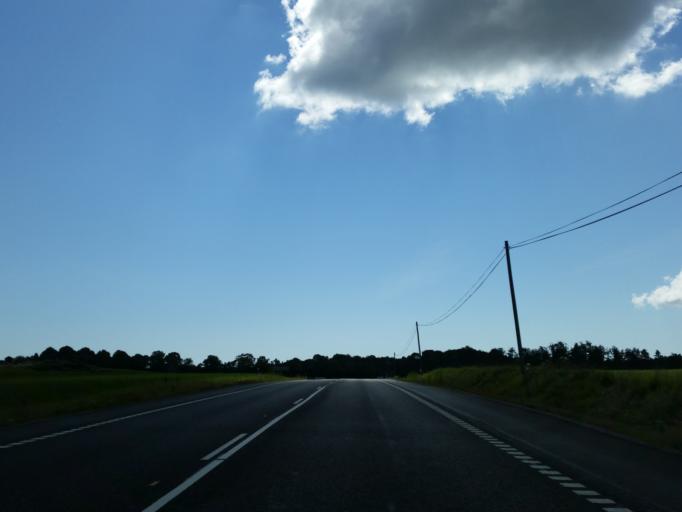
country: SE
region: Soedermanland
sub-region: Trosa Kommun
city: Vagnharad
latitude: 59.0118
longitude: 17.5954
